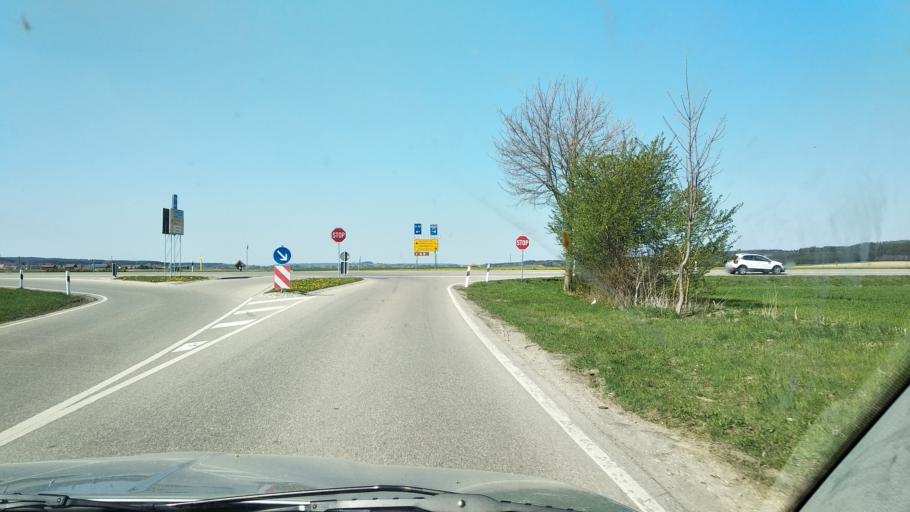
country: DE
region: Bavaria
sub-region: Swabia
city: Stetten
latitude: 48.0458
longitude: 10.4322
